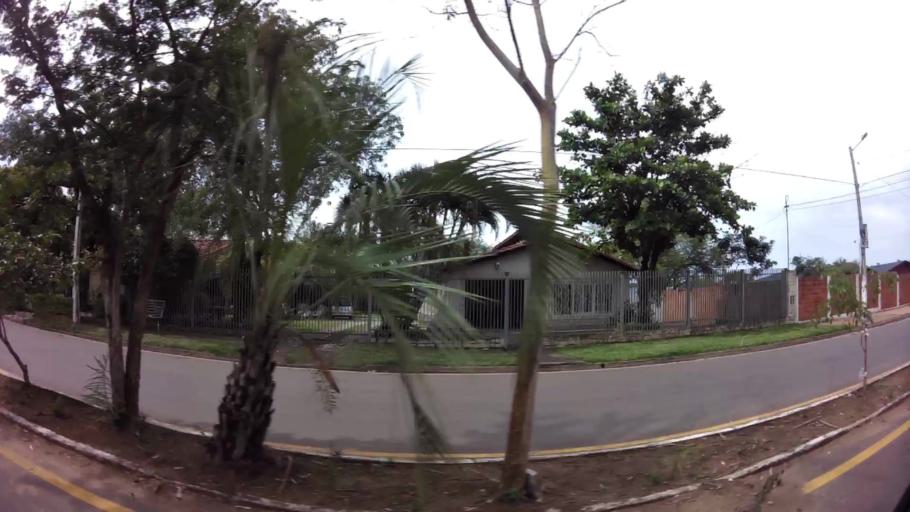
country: PY
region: Central
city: Limpio
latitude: -25.1751
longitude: -57.4764
